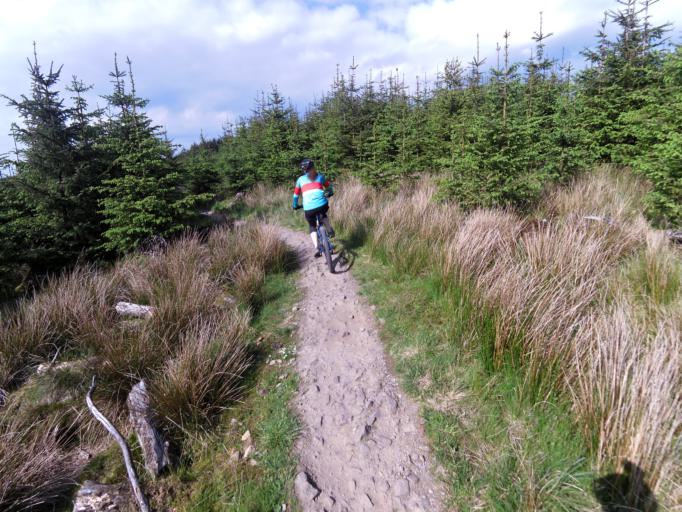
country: GB
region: England
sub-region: North Yorkshire
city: Settle
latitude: 54.0185
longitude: -2.3703
